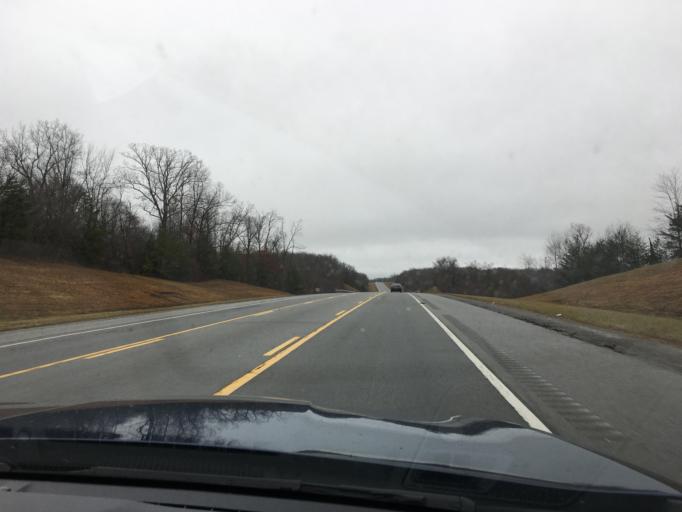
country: US
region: Tennessee
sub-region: Cumberland County
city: Crossville
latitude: 35.9396
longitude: -84.9989
